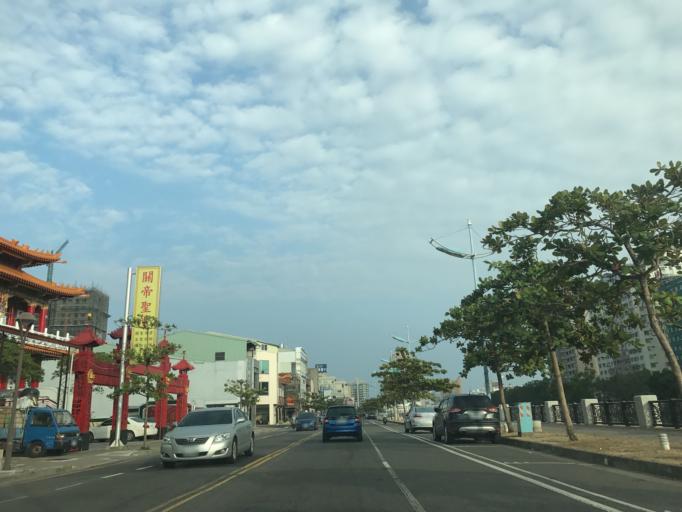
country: TW
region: Taiwan
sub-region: Tainan
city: Tainan
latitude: 22.9985
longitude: 120.1805
